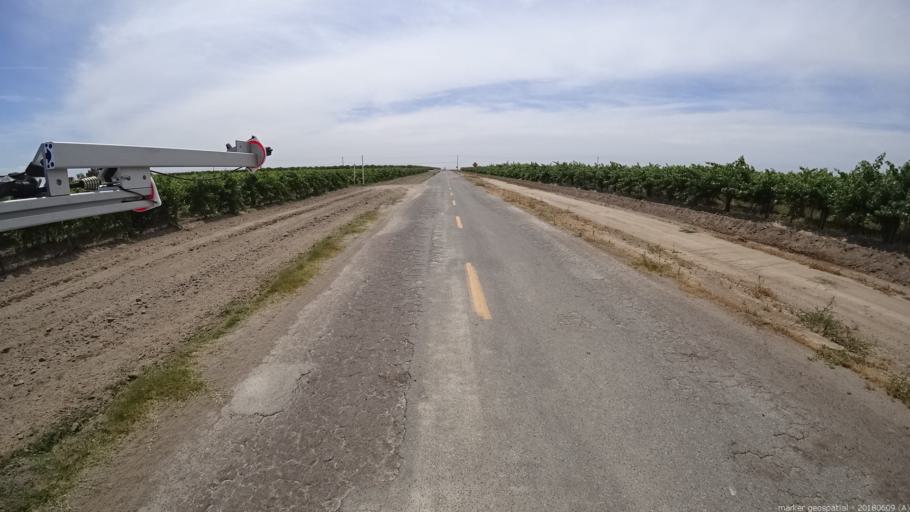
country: US
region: California
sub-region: Madera County
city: Madera
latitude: 36.9093
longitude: -120.1623
